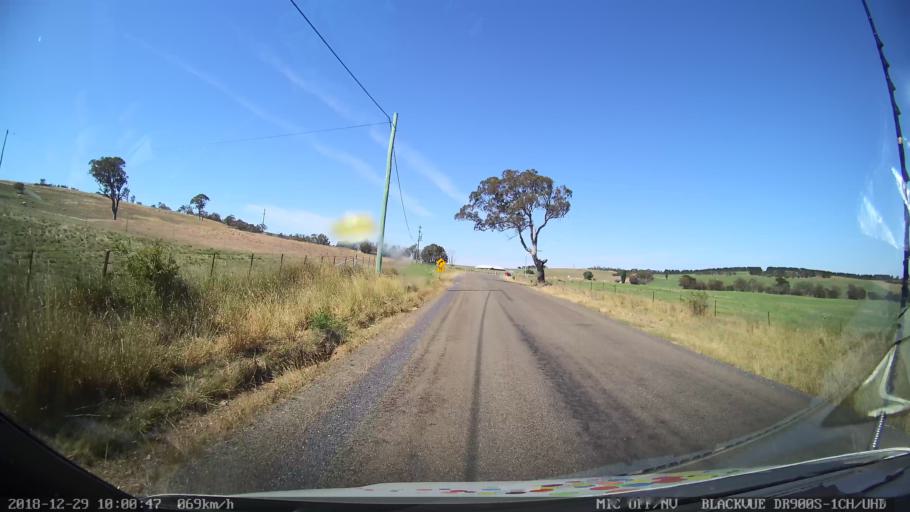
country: AU
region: New South Wales
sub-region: Goulburn Mulwaree
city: Goulburn
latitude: -34.7951
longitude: 149.4833
